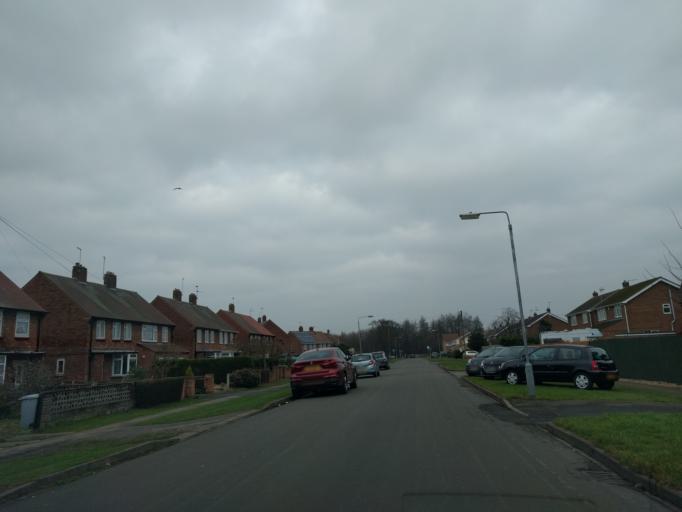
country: GB
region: England
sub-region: Nottinghamshire
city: Newark on Trent
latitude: 53.0926
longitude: -0.7945
